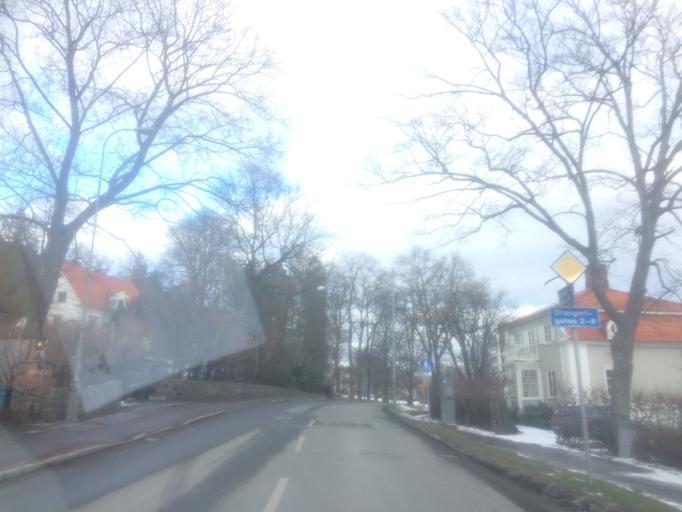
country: SE
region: Vaestra Goetaland
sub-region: Goteborg
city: Goeteborg
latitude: 57.7000
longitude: 11.9995
